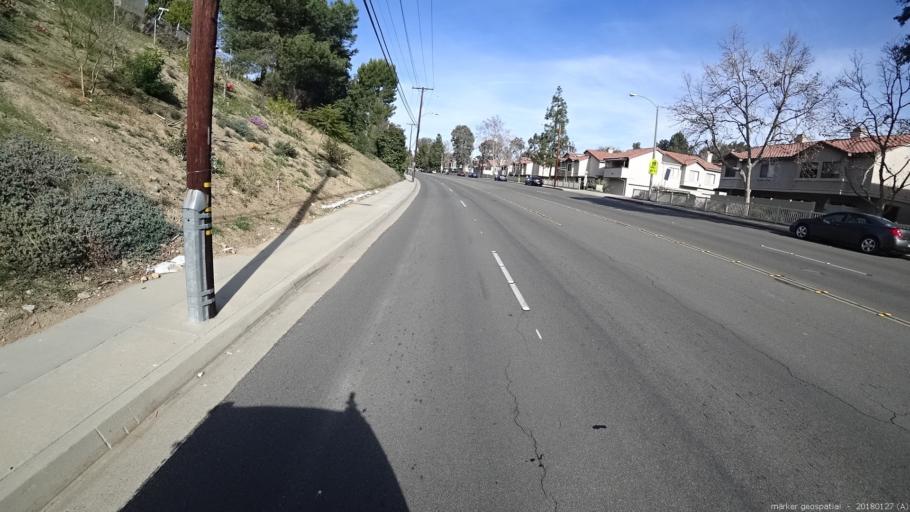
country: US
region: California
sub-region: Los Angeles County
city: Diamond Bar
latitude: 34.0297
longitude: -117.7962
